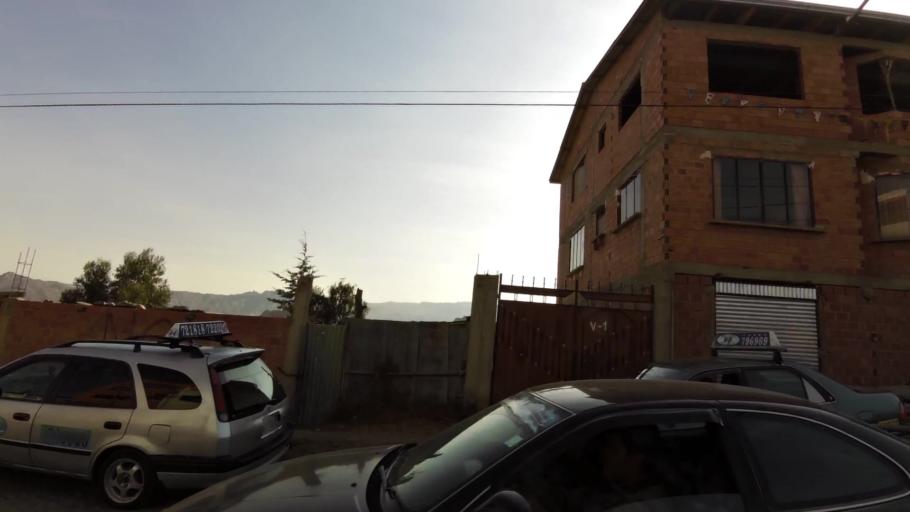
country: BO
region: La Paz
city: La Paz
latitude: -16.5168
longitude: -68.0845
